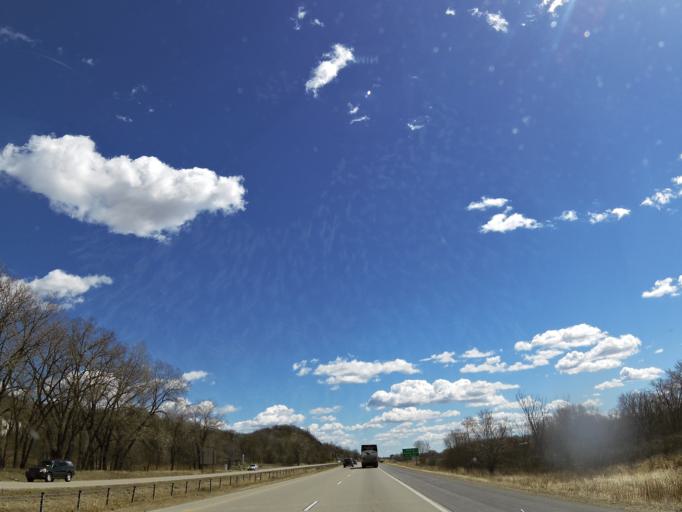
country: US
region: Minnesota
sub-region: Washington County
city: Saint Paul Park
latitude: 44.8439
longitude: -92.9791
